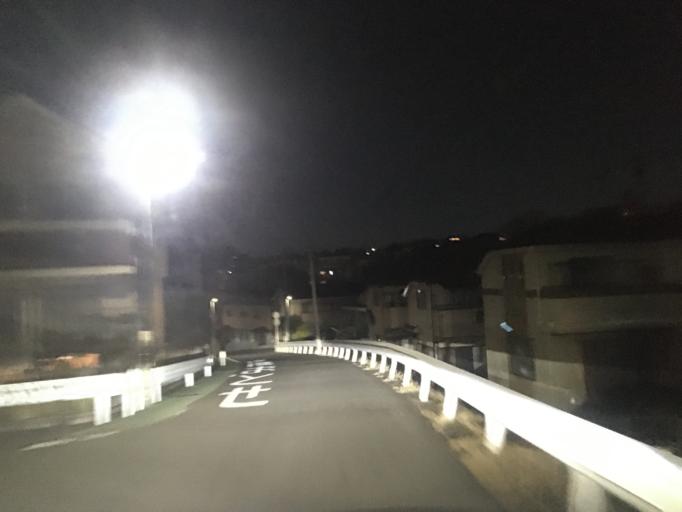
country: JP
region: Tokyo
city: Chofugaoka
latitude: 35.6014
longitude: 139.5224
